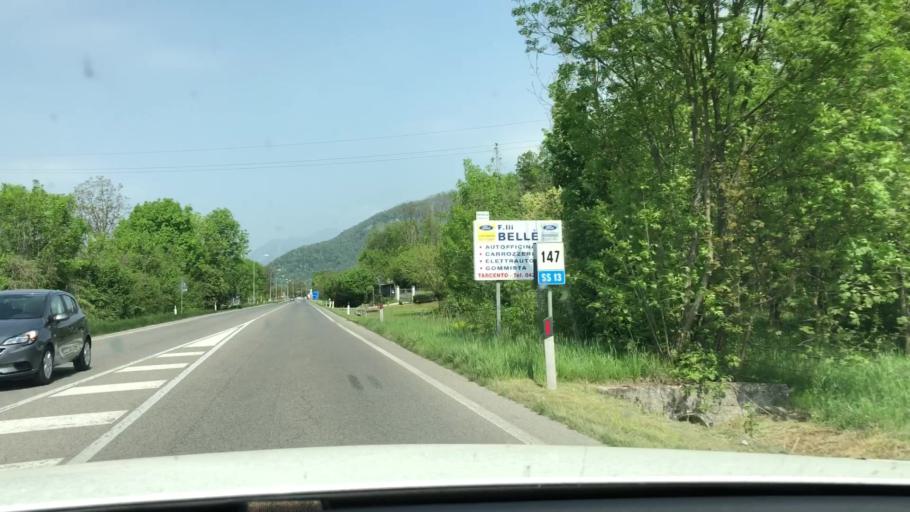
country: IT
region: Friuli Venezia Giulia
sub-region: Provincia di Udine
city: Magnano in Riviera
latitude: 46.2110
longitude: 13.1849
